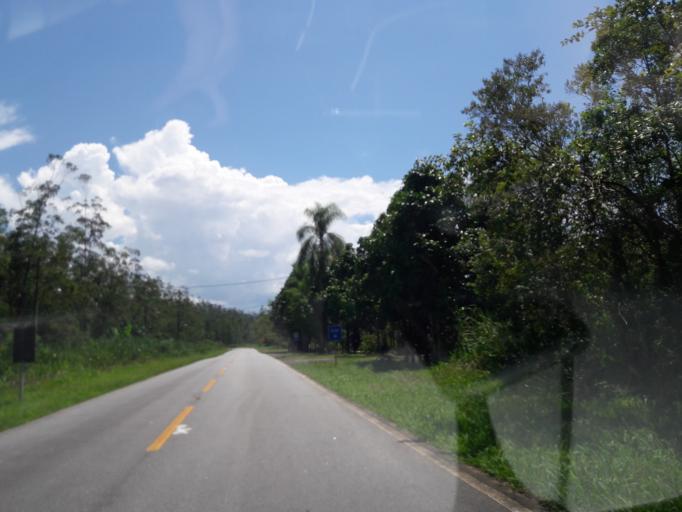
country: BR
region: Parana
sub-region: Antonina
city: Antonina
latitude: -25.5253
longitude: -48.7792
